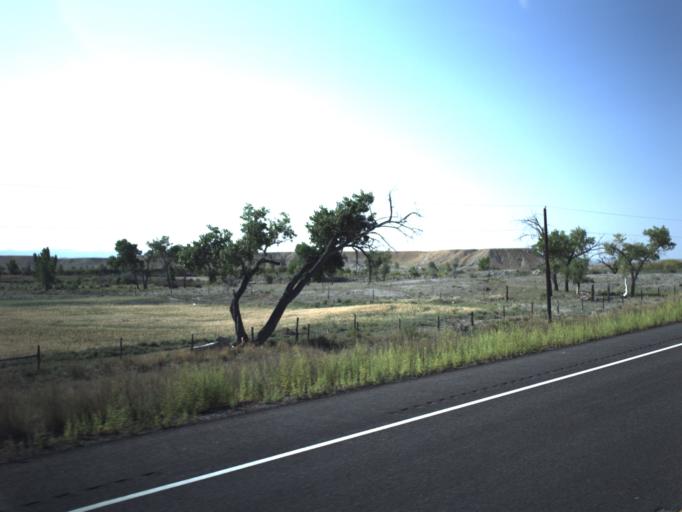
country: US
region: Utah
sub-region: Emery County
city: Huntington
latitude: 39.2845
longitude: -110.9734
